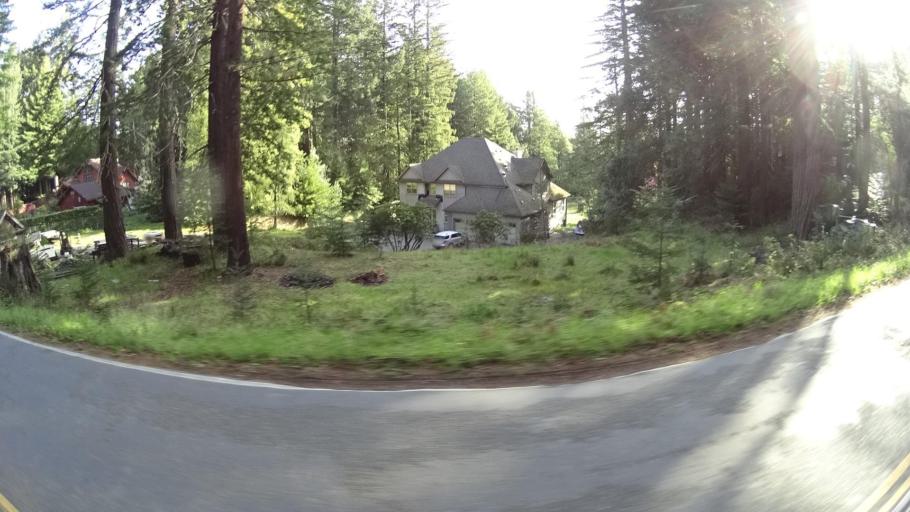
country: US
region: California
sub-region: Humboldt County
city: Bayside
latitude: 40.7564
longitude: -123.9892
